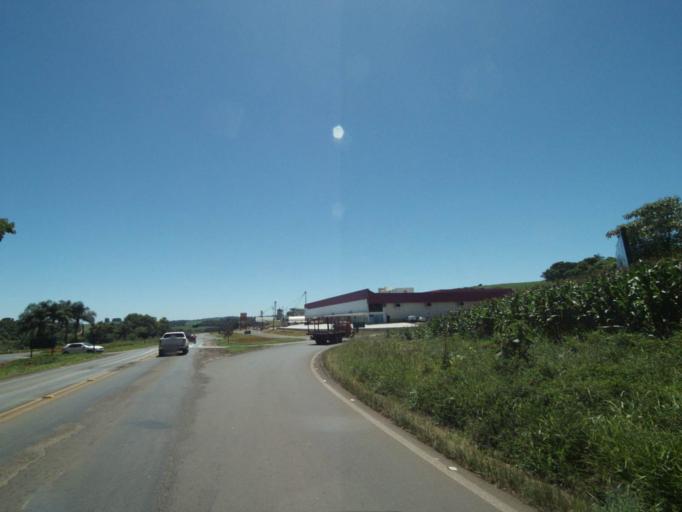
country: BR
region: Santa Catarina
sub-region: Sao Lourenco Do Oeste
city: Sao Lourenco dOeste
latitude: -26.2586
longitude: -52.7883
